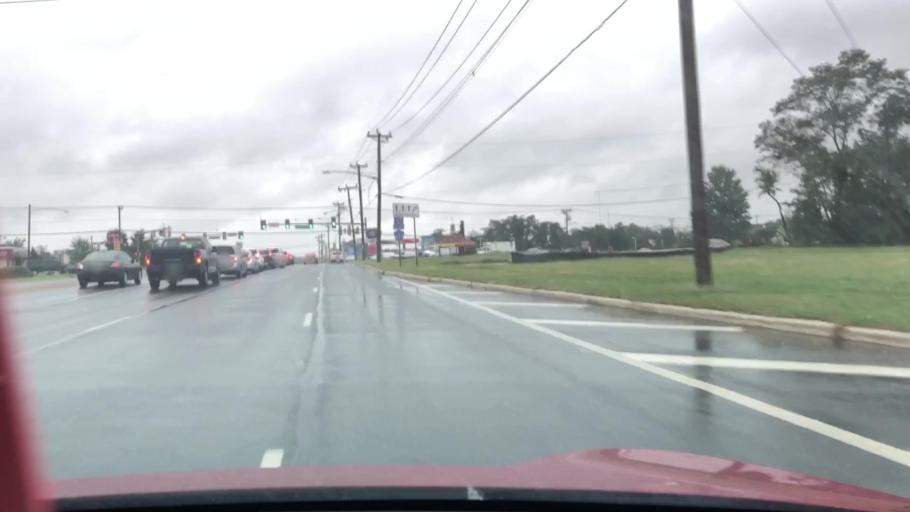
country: US
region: New Jersey
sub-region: Atlantic County
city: Northfield
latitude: 39.3955
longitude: -74.5601
